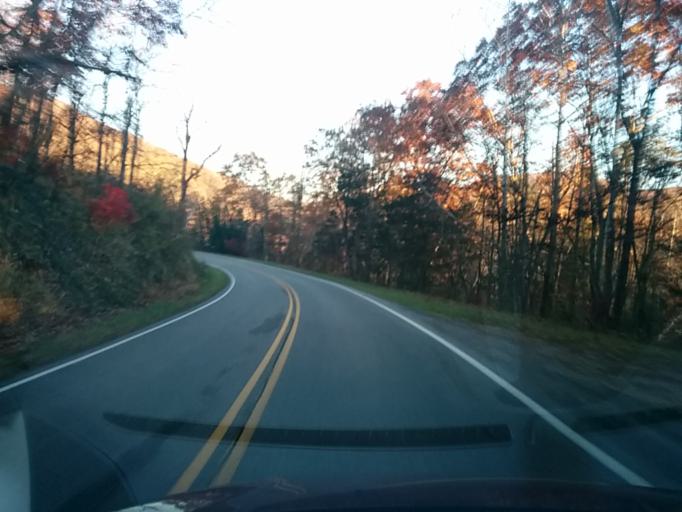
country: US
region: Virginia
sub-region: Rockbridge County
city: East Lexington
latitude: 37.9063
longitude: -79.4220
